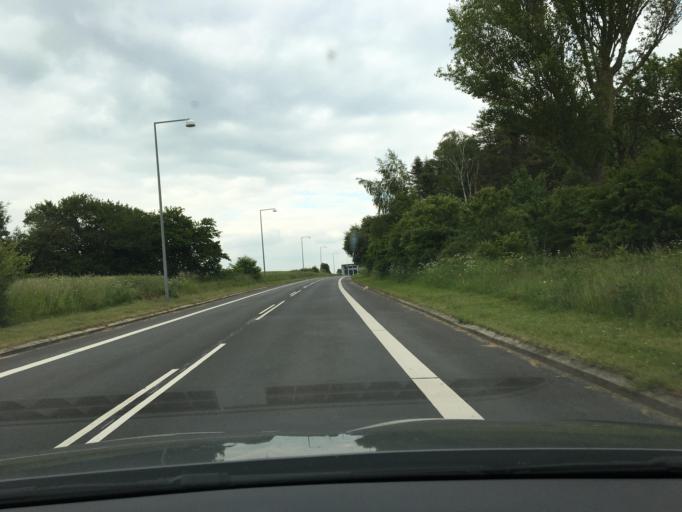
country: DK
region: South Denmark
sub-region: Assens Kommune
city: Assens
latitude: 55.2810
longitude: 9.9127
